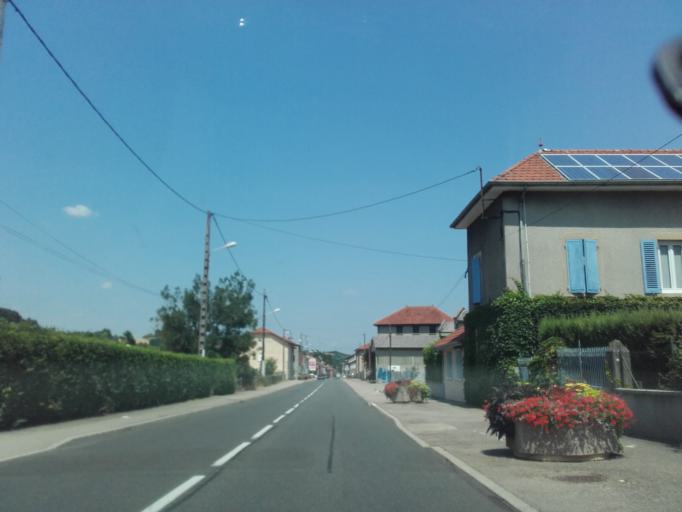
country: FR
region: Rhone-Alpes
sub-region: Departement de l'Isere
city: Nivolas-Vermelle
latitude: 45.5529
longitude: 5.3063
